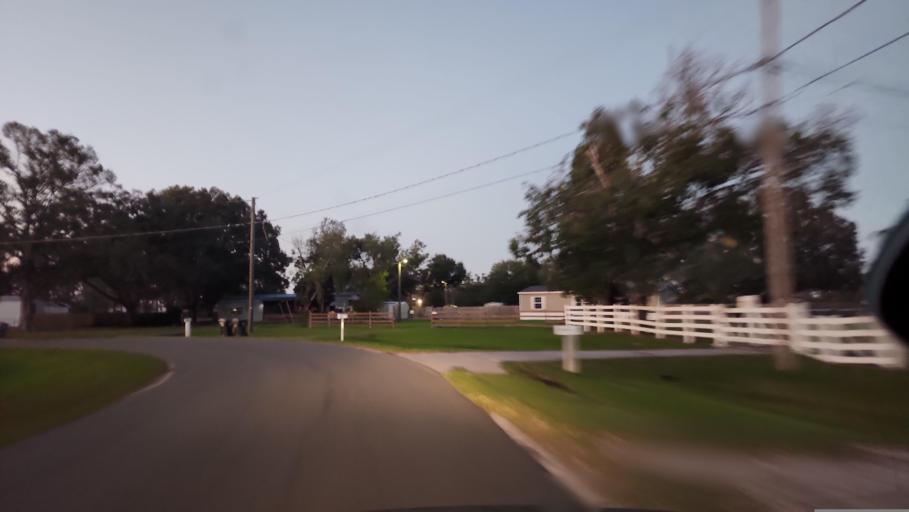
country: US
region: Florida
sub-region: Hillsborough County
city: Boyette
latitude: 27.8127
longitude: -82.2747
